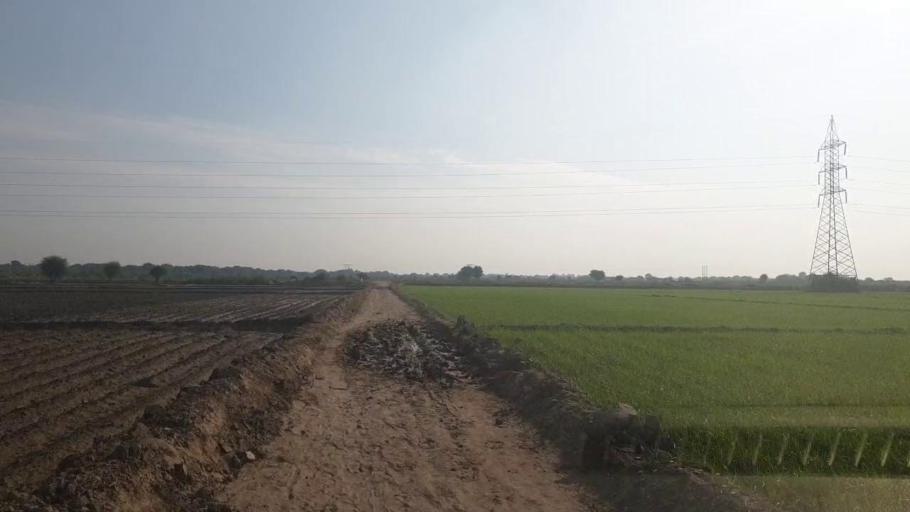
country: PK
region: Sindh
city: Tando Jam
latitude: 25.4280
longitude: 68.4771
